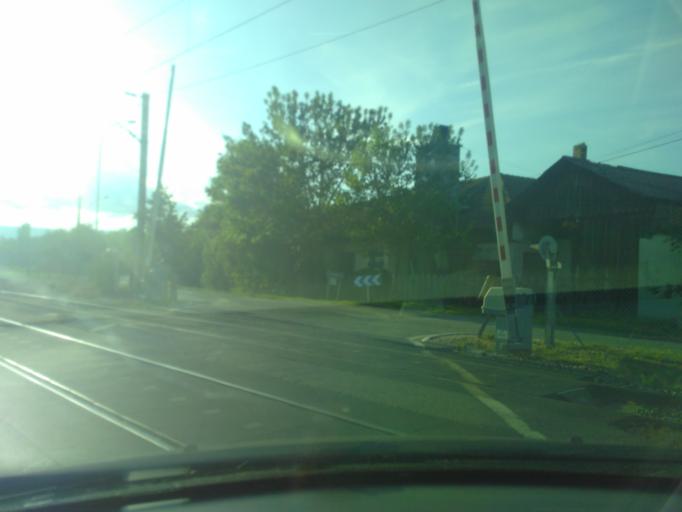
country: FR
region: Rhone-Alpes
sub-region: Departement de la Haute-Savoie
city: Saint-Julien-en-Genevois
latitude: 46.1419
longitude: 6.0918
